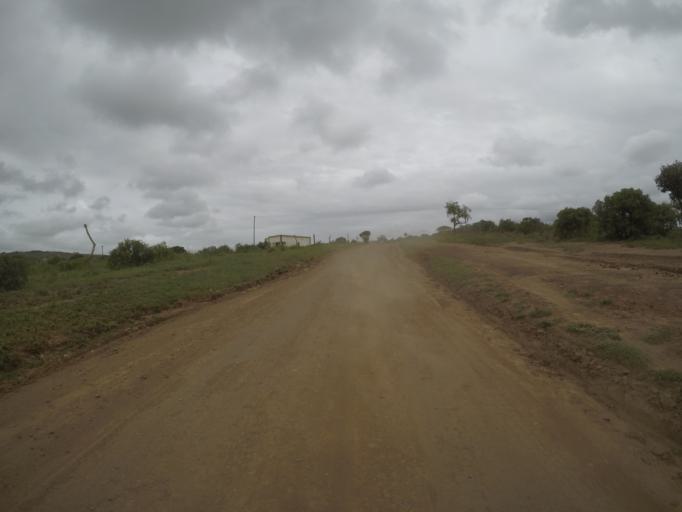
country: ZA
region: KwaZulu-Natal
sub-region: uThungulu District Municipality
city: Empangeni
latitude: -28.5944
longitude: 31.8405
